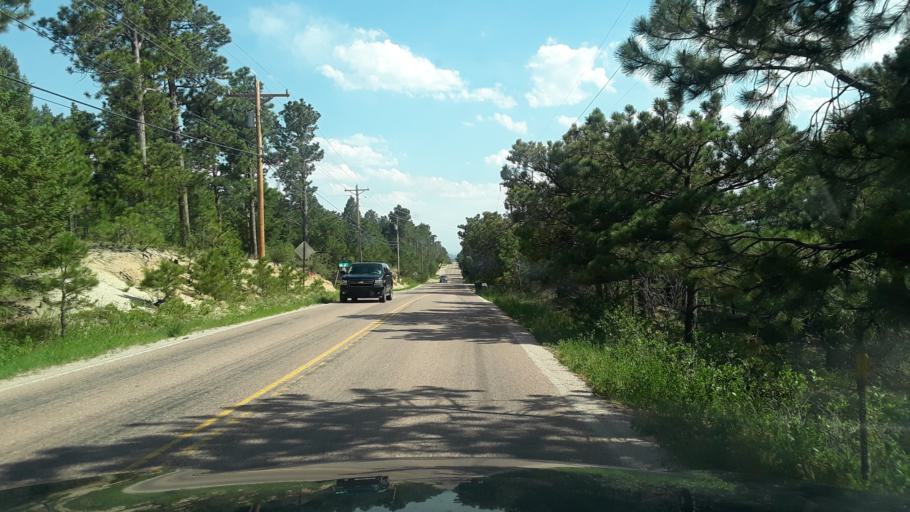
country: US
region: Colorado
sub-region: El Paso County
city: Gleneagle
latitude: 39.0475
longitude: -104.7849
